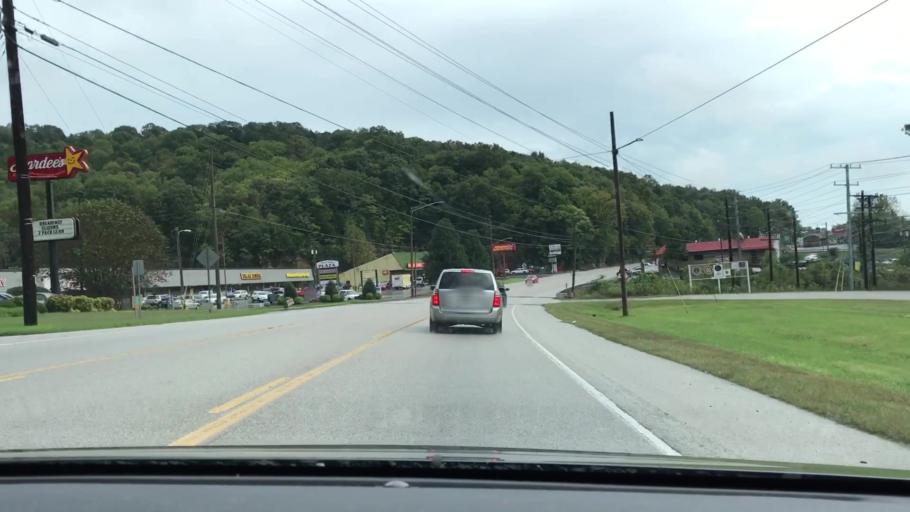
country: US
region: Tennessee
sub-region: Smith County
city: Carthage
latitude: 36.2666
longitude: -85.9594
